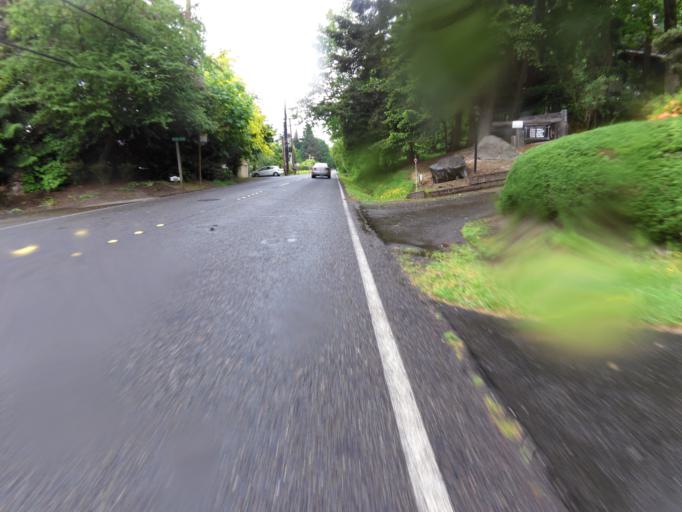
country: US
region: Washington
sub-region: King County
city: Mercer Island
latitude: 47.5314
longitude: -122.2193
